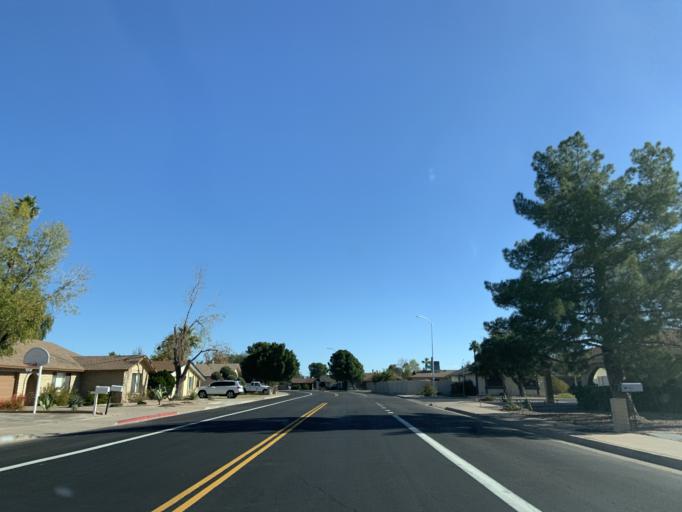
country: US
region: Arizona
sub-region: Maricopa County
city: San Carlos
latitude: 33.3659
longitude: -111.8655
